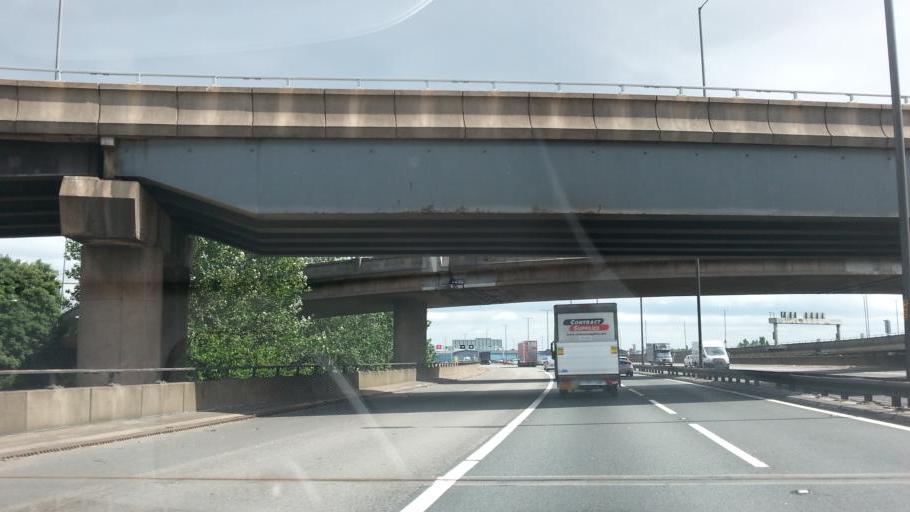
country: GB
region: England
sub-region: City and Borough of Birmingham
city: Birmingham
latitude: 52.5114
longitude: -1.8652
